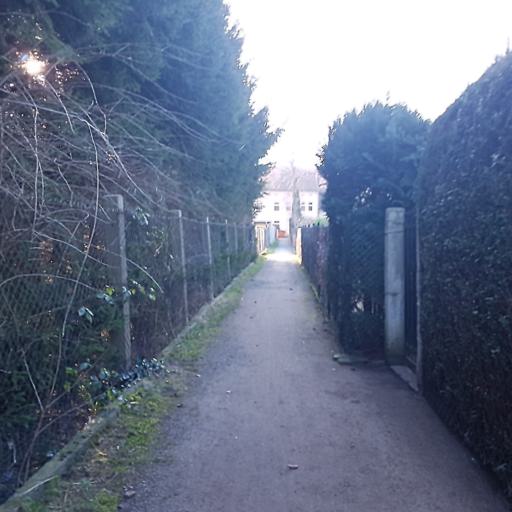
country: DE
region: Brandenburg
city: Bad Liebenwerda
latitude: 51.5175
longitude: 13.3919
